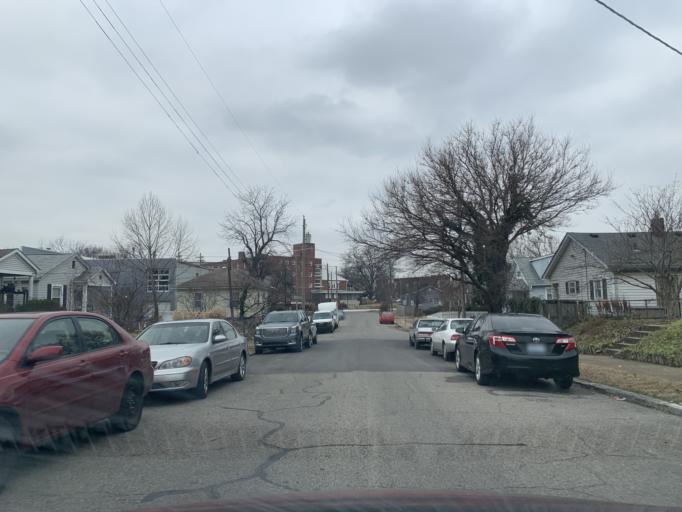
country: US
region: Kentucky
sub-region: Jefferson County
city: Audubon Park
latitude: 38.2262
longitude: -85.7404
